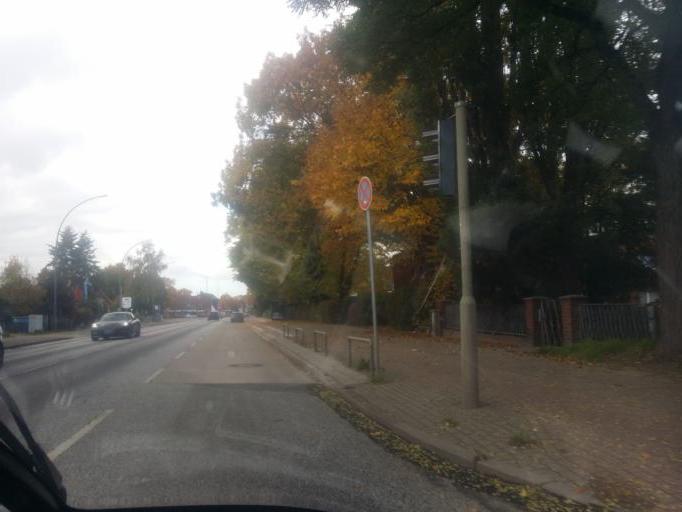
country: DE
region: Schleswig-Holstein
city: Halstenbek
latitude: 53.5981
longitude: 9.8579
